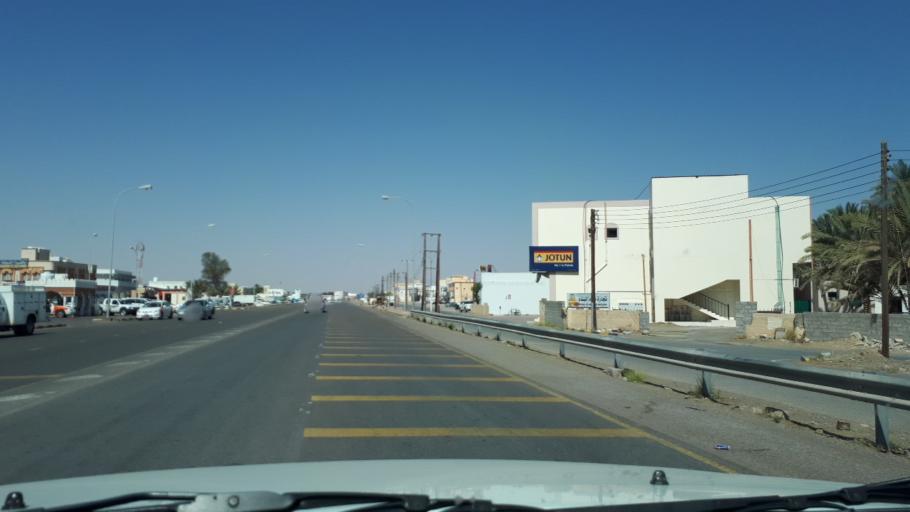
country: OM
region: Ash Sharqiyah
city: Badiyah
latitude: 22.2244
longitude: 59.2049
